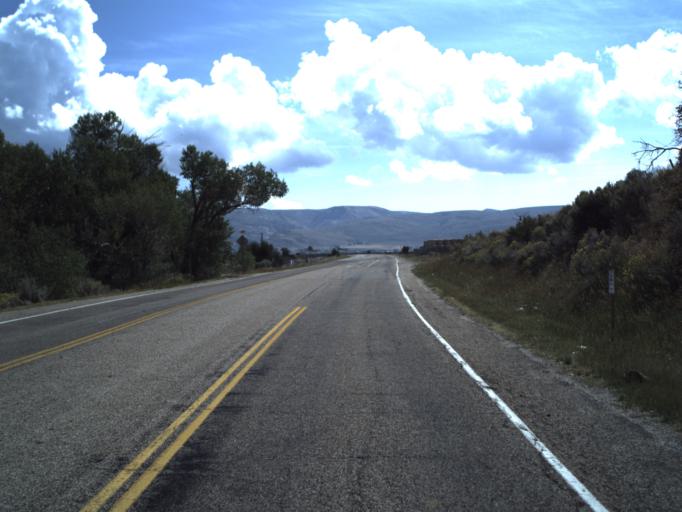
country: US
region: Utah
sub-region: Rich County
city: Randolph
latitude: 41.8474
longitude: -111.3524
